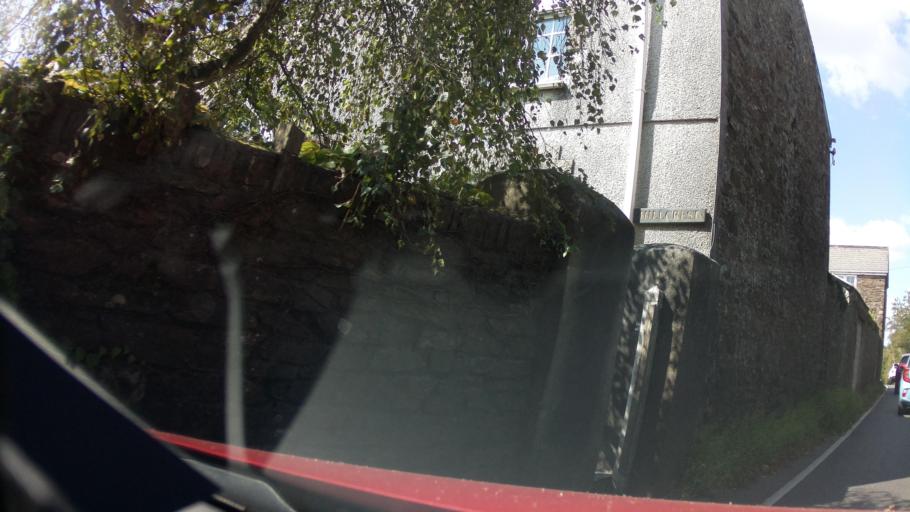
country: GB
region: England
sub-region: Cornwall
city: Pillaton
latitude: 50.4684
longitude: -4.2709
